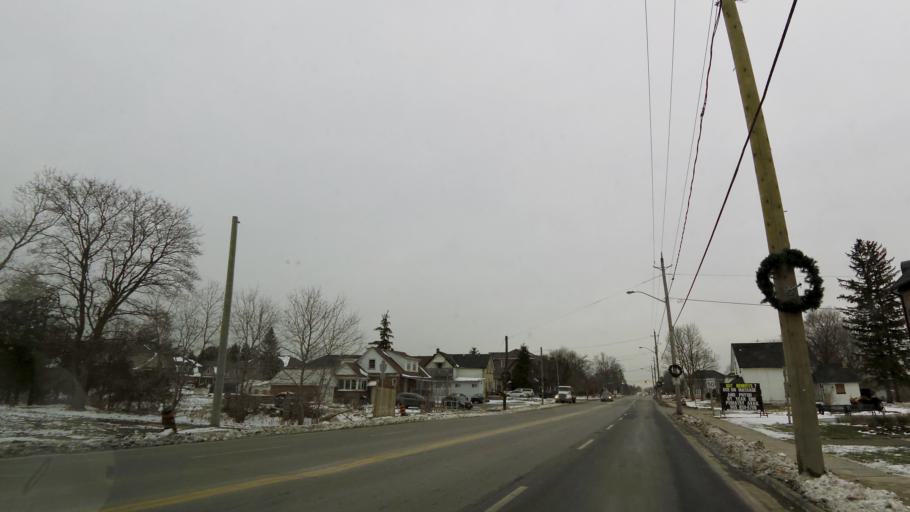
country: CA
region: Ontario
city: Vaughan
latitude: 43.9030
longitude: -79.6529
